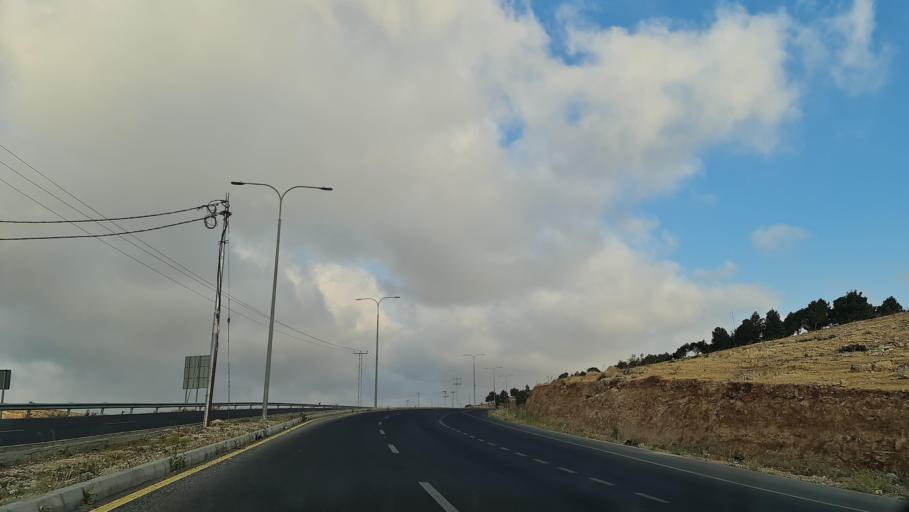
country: JO
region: Zarqa
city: Russeifa
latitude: 32.0923
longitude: 35.9717
